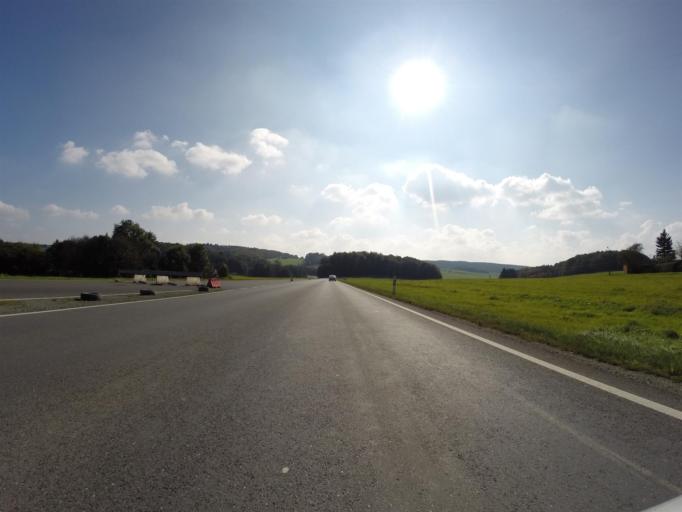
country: DE
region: Thuringia
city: Schleiz
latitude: 50.5664
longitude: 11.8080
